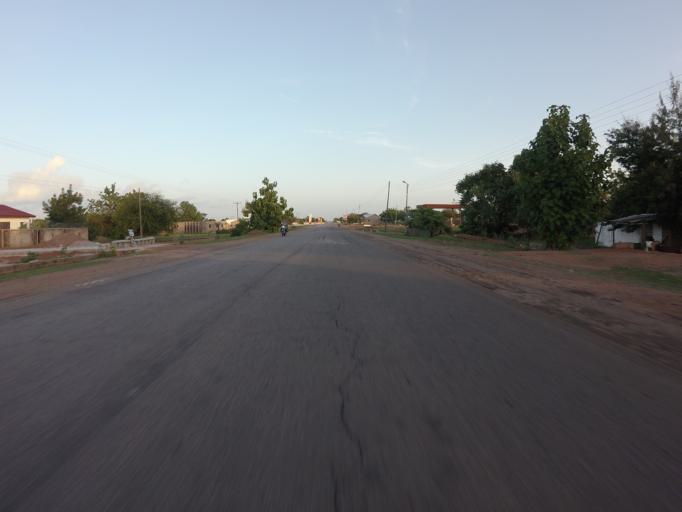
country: GH
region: Upper East
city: Navrongo
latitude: 10.9552
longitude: -1.0970
